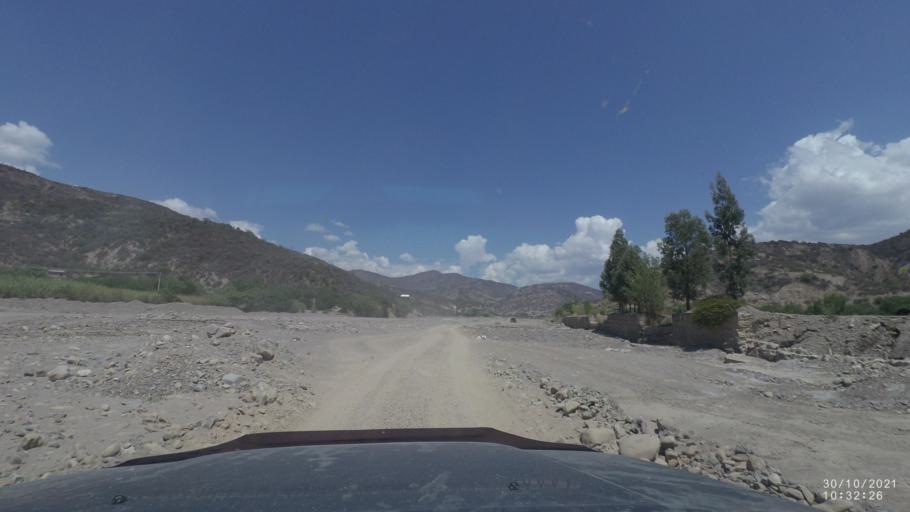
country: BO
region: Cochabamba
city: Sipe Sipe
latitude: -17.5474
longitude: -66.4124
